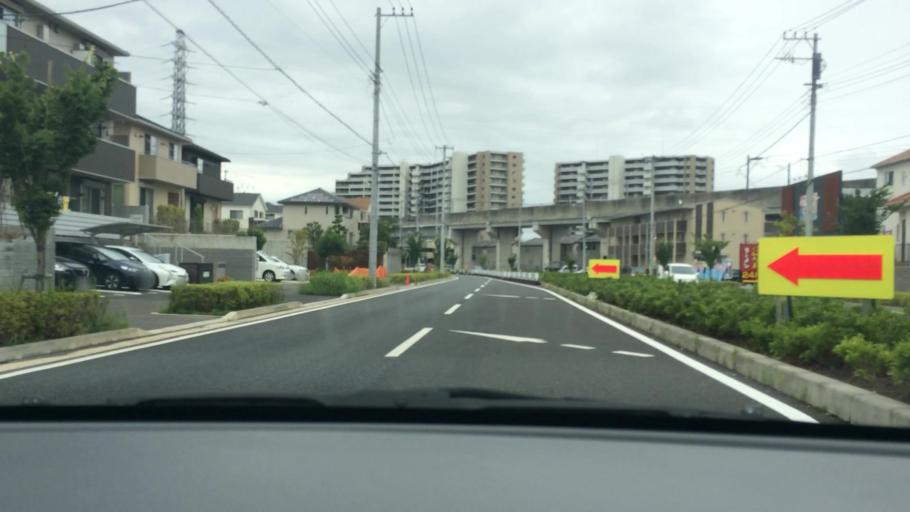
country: JP
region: Chiba
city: Nagareyama
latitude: 35.8777
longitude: 139.9300
